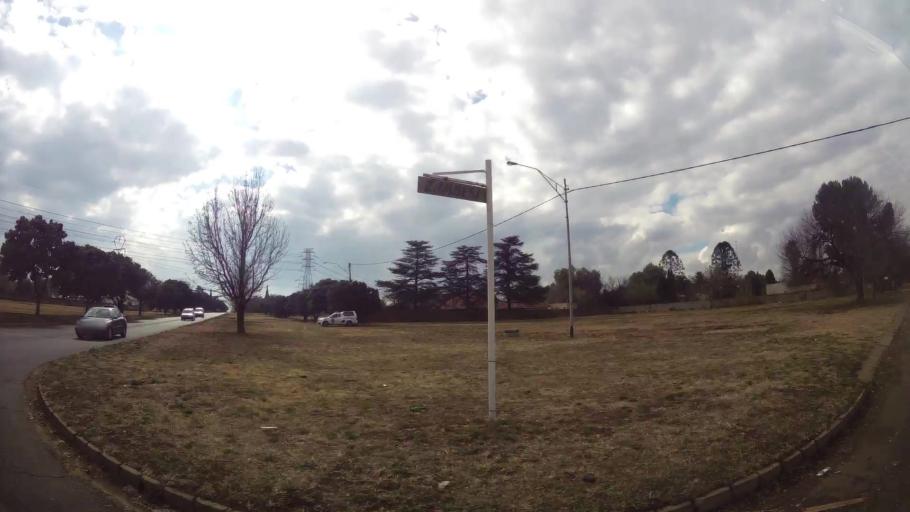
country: ZA
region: Gauteng
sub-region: Sedibeng District Municipality
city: Vereeniging
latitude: -26.6513
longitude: 27.9684
